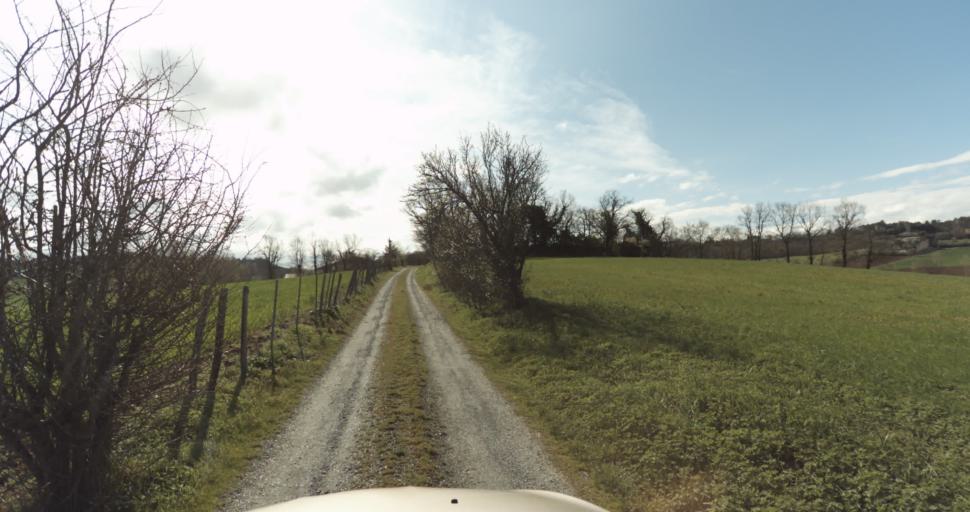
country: FR
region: Midi-Pyrenees
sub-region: Departement du Tarn
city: Puygouzon
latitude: 43.8749
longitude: 2.1772
